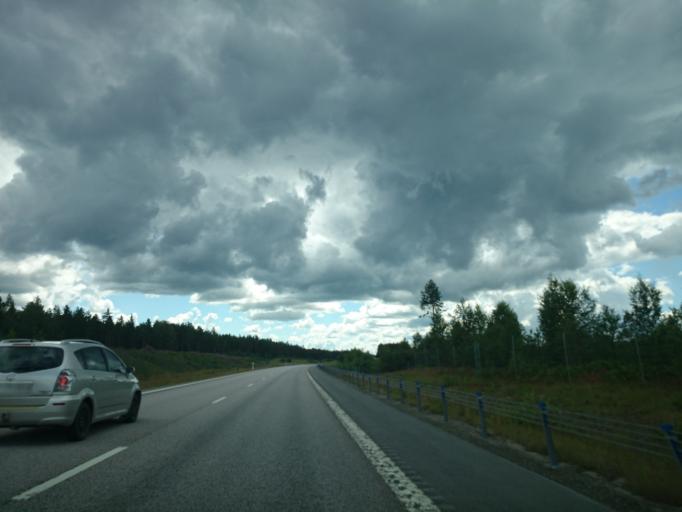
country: SE
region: Uppsala
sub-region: Tierps Kommun
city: Tierp
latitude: 60.3104
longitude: 17.5212
